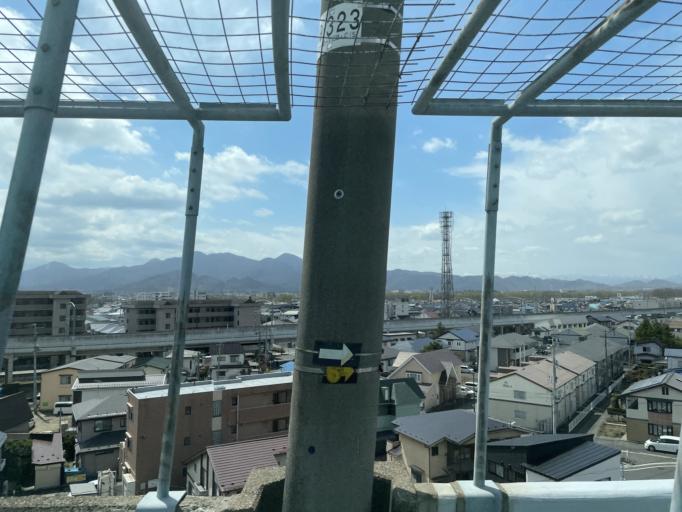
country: JP
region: Iwate
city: Morioka-shi
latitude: 39.7089
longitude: 141.1281
